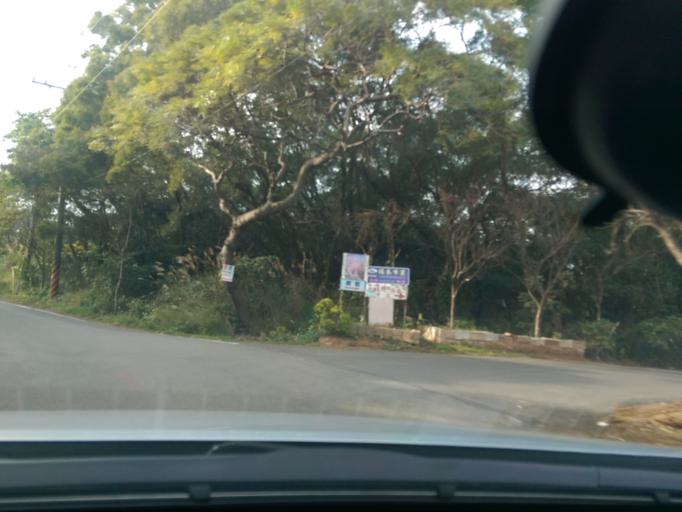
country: TW
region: Taiwan
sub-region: Taoyuan
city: Taoyuan
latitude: 25.0907
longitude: 121.3673
